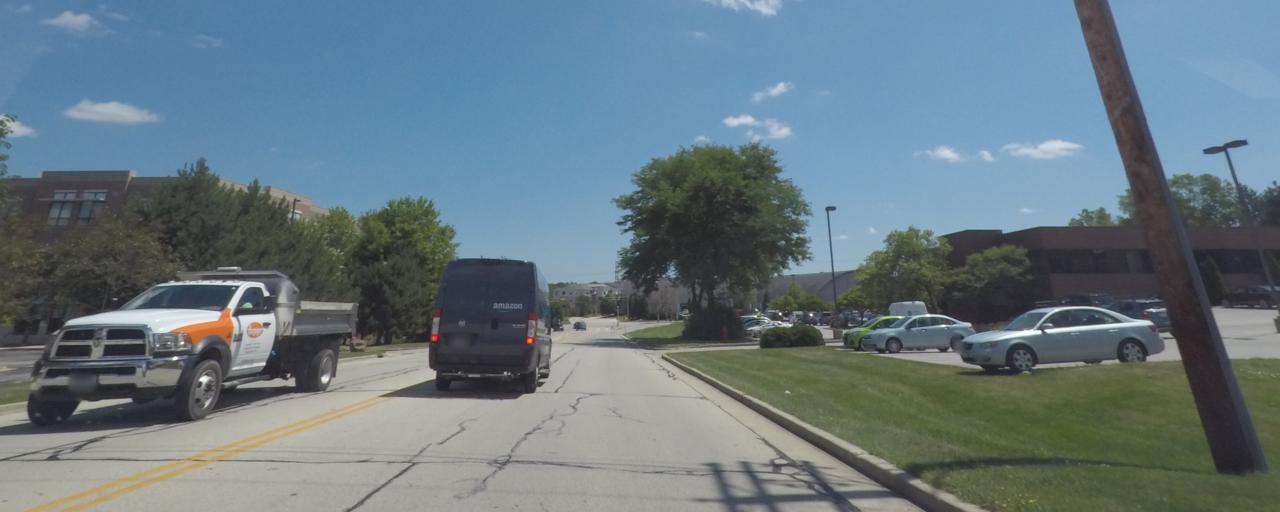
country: US
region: Wisconsin
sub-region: Waukesha County
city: Brookfield
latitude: 43.0384
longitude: -88.1687
